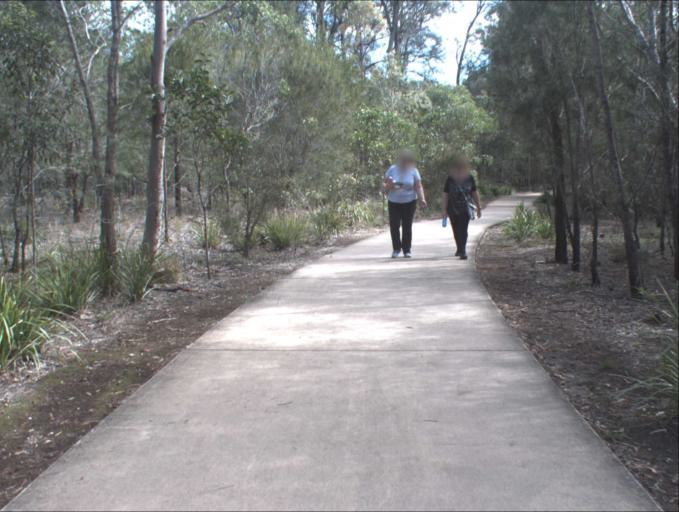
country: AU
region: Queensland
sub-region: Logan
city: Woodridge
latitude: -27.6645
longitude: 153.0738
